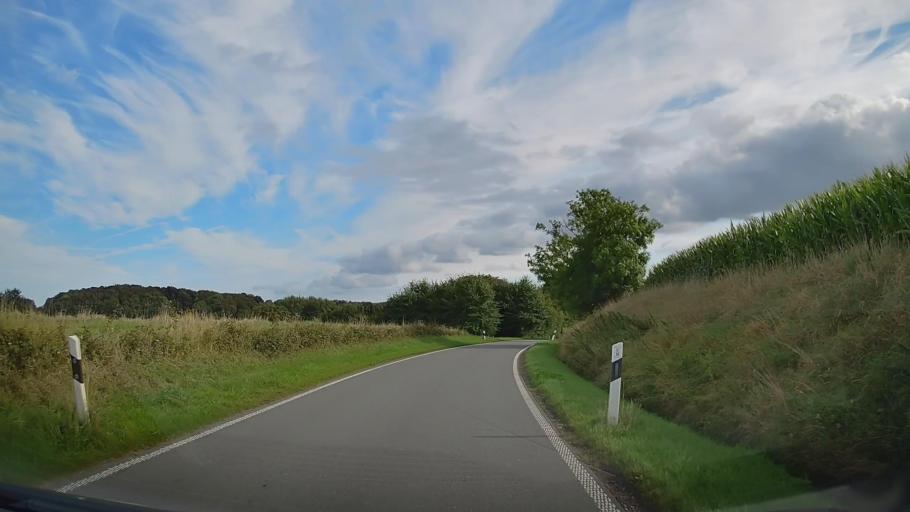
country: DE
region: Schleswig-Holstein
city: Westerholz
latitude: 54.8073
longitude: 9.6836
